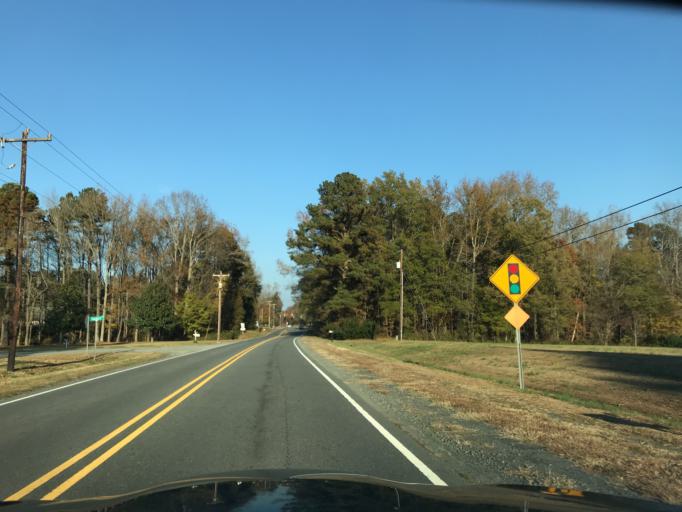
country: US
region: North Carolina
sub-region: Granville County
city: Butner
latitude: 36.0979
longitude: -78.7347
